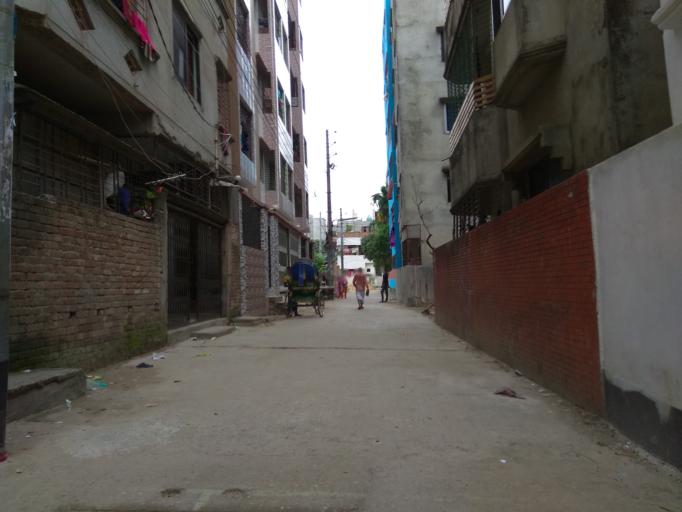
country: BD
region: Dhaka
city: Tungi
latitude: 23.8153
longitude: 90.3773
